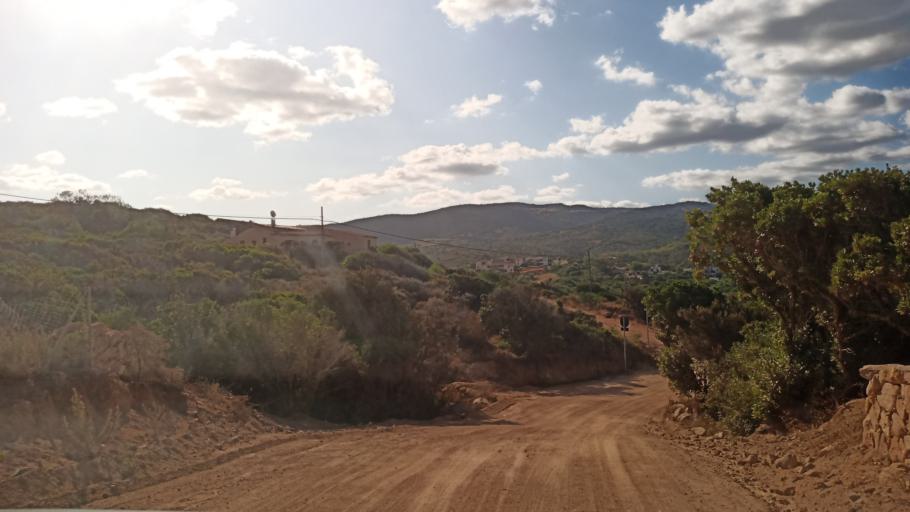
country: IT
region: Sardinia
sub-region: Provincia di Olbia-Tempio
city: Trinita d'Agultu
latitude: 41.0192
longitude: 8.8904
